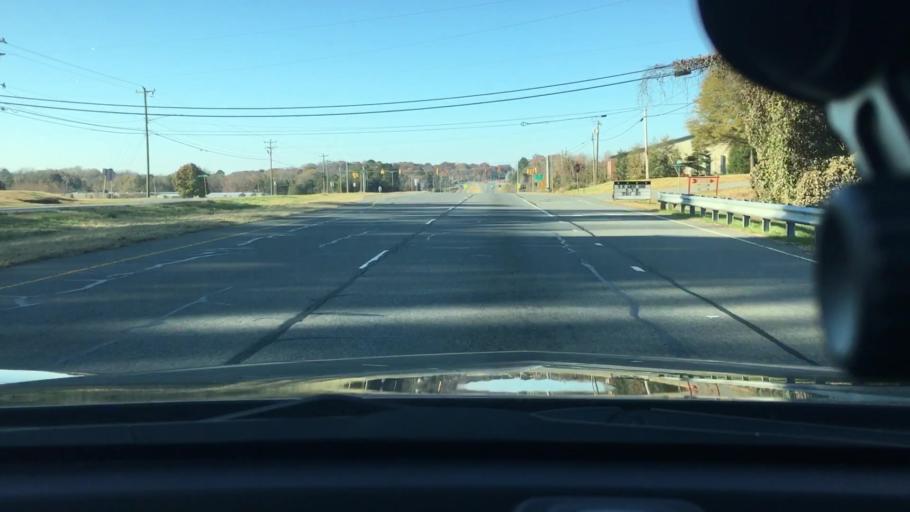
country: US
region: North Carolina
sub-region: Cabarrus County
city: Concord
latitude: 35.3656
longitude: -80.5822
